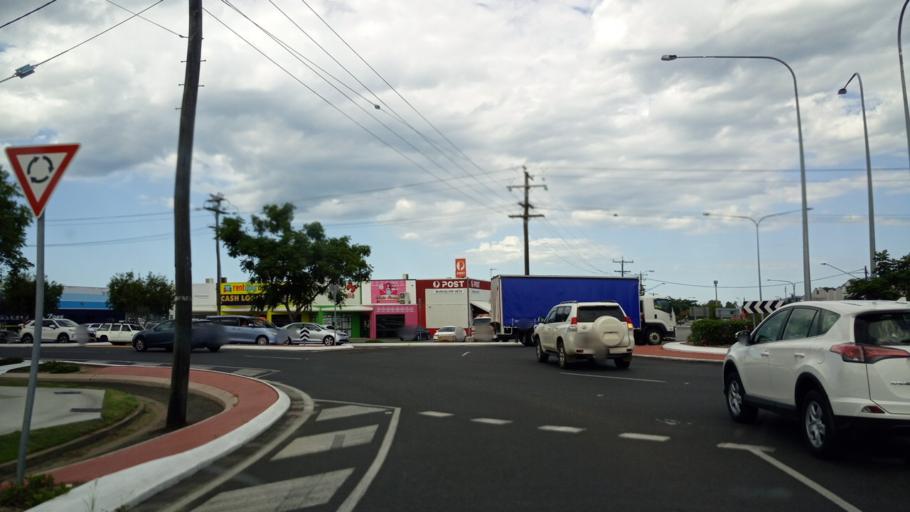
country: AU
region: Queensland
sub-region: Cairns
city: Cairns
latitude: -16.9335
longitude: 145.7607
